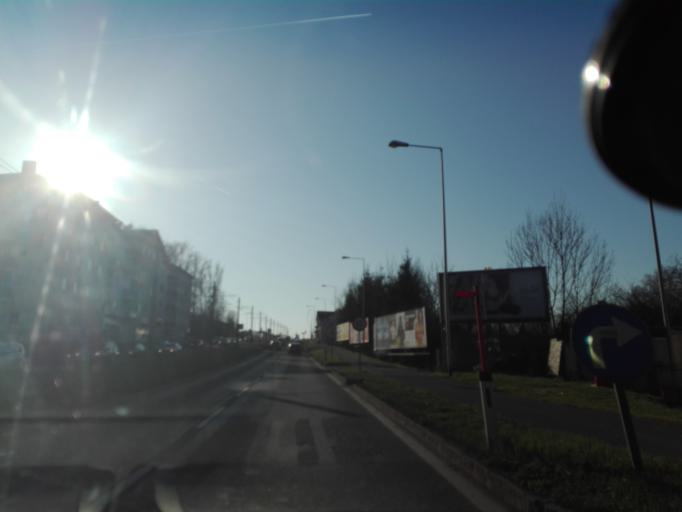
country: AT
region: Upper Austria
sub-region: Politischer Bezirk Linz-Land
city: Leonding
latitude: 48.2747
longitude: 14.2727
